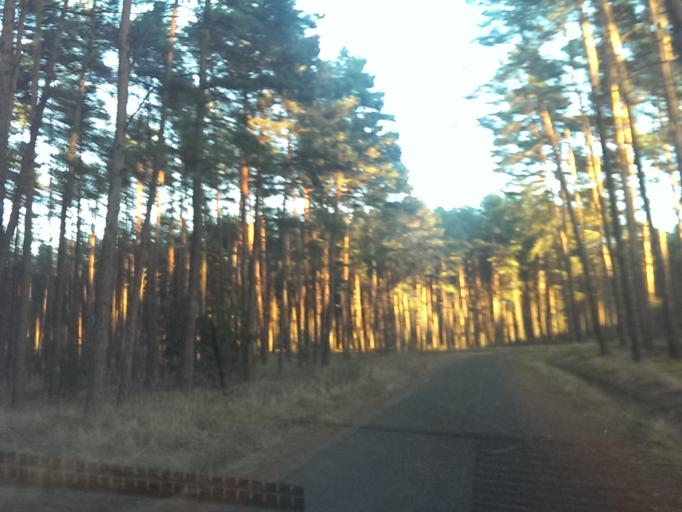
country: PL
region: Kujawsko-Pomorskie
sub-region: Powiat nakielski
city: Naklo nad Notecia
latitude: 53.0473
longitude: 17.5881
